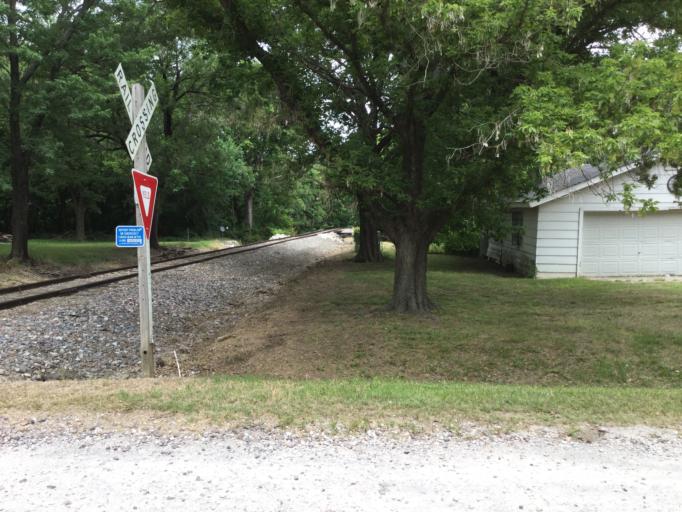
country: US
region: Kansas
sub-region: Montgomery County
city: Independence
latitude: 37.2174
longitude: -95.7176
